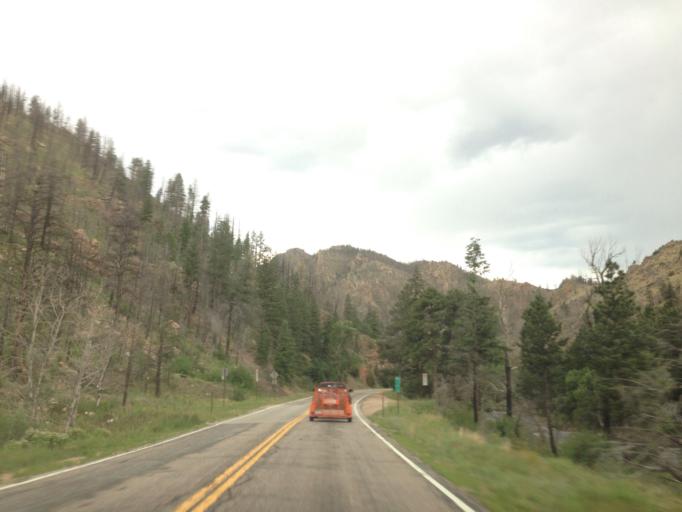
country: US
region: Colorado
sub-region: Larimer County
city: Laporte
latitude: 40.6877
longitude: -105.4326
